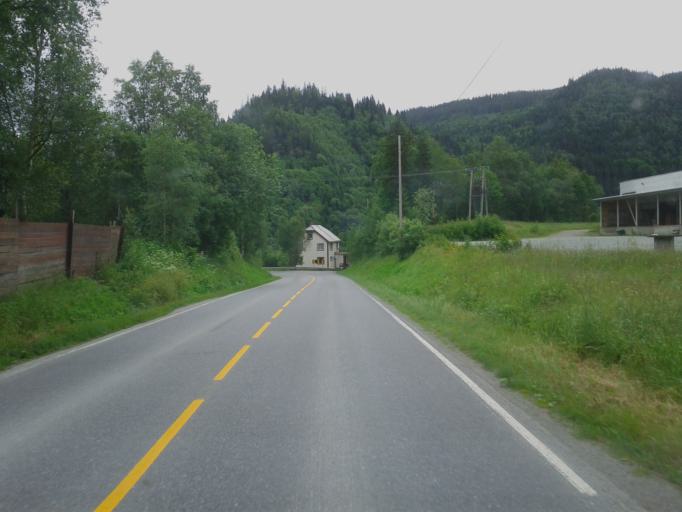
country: NO
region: Sor-Trondelag
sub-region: Midtre Gauldal
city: Storen
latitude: 62.9930
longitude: 10.4912
